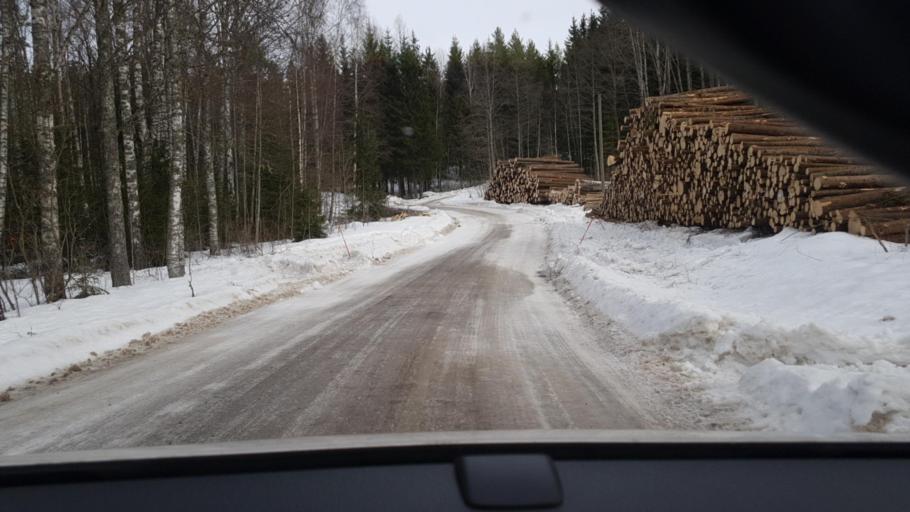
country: SE
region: Vaermland
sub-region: Eda Kommun
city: Amotfors
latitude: 59.7869
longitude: 12.3750
